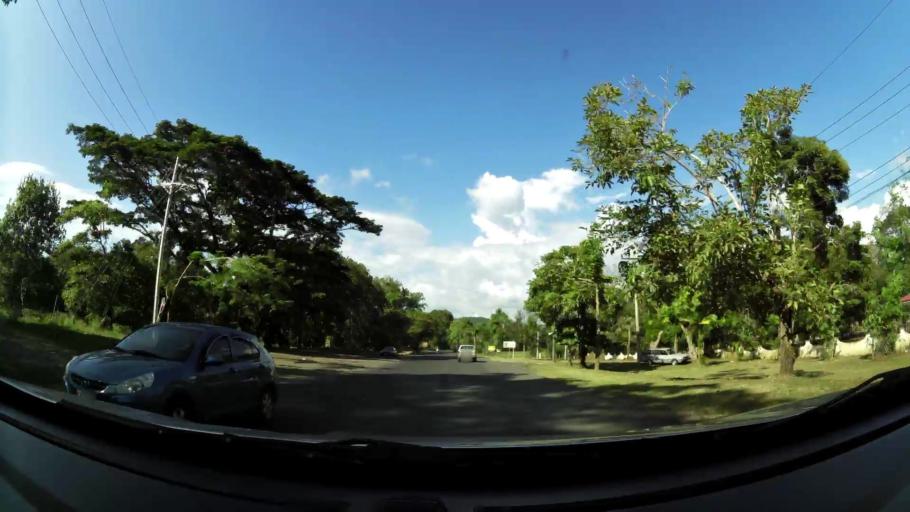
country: CR
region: Puntarenas
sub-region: Canton de Garabito
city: Jaco
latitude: 9.6035
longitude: -84.6157
